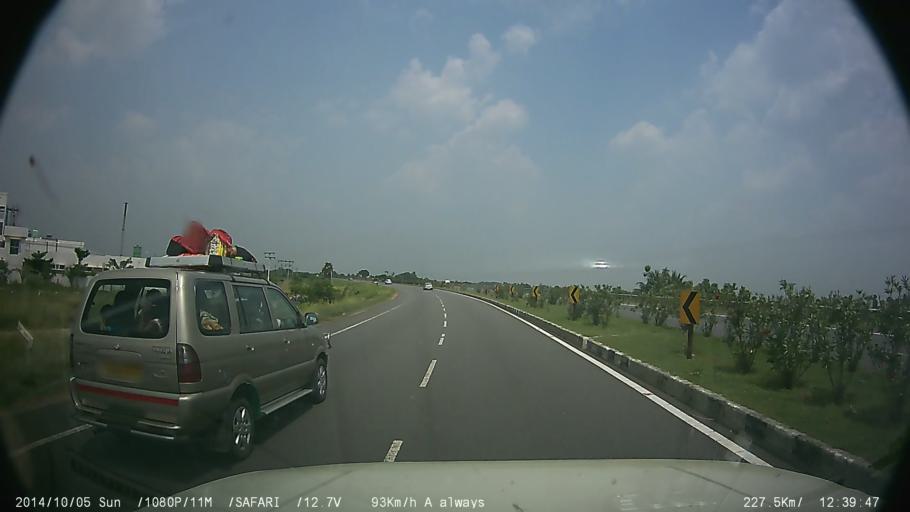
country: IN
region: Tamil Nadu
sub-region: Cuddalore
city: Vriddhachalam
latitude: 11.6850
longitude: 79.3104
